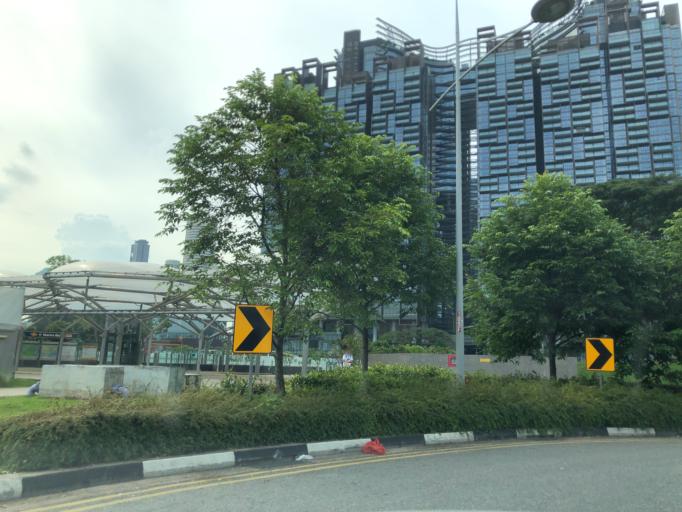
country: SG
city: Singapore
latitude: 1.2761
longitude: 103.8553
